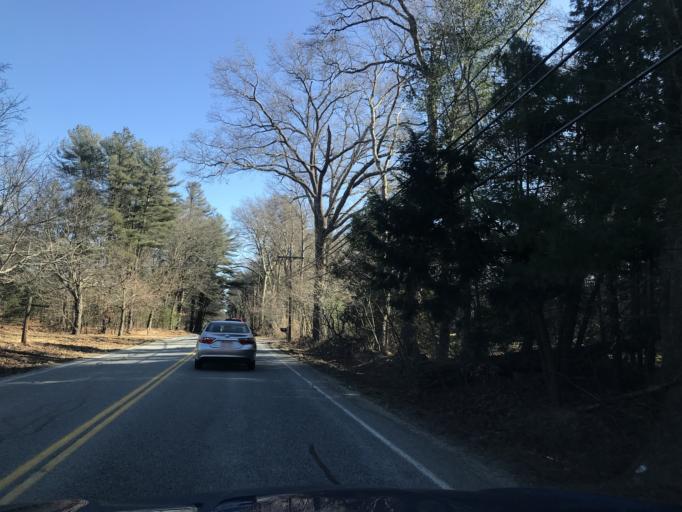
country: US
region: Massachusetts
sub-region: Essex County
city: Groveland
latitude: 42.7119
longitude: -71.0391
